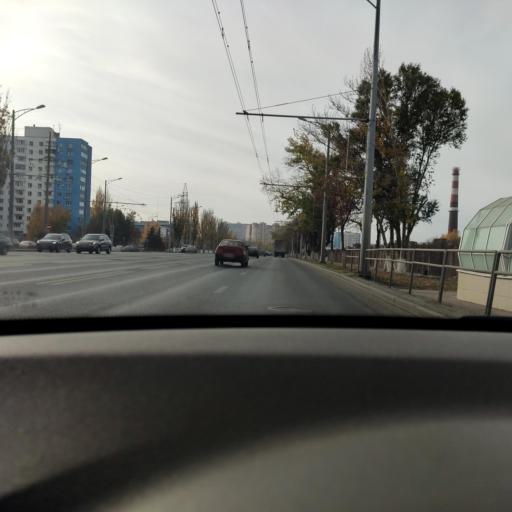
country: RU
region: Samara
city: Samara
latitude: 53.2368
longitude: 50.2020
